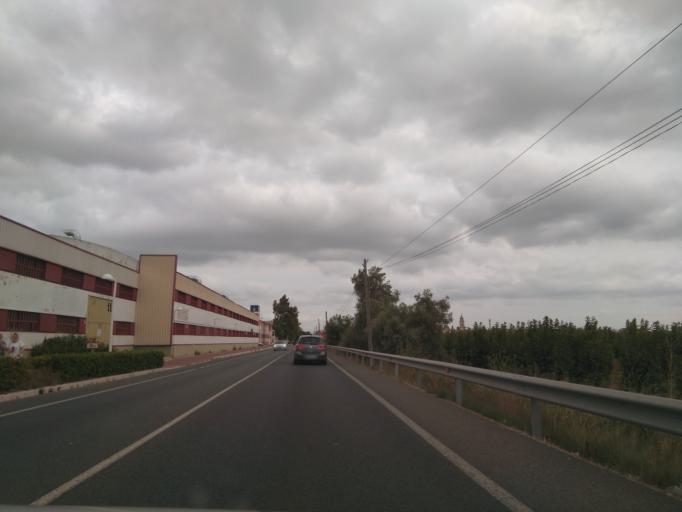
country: ES
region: Valencia
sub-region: Provincia de Valencia
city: L'Alcudia
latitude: 39.2058
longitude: -0.5088
